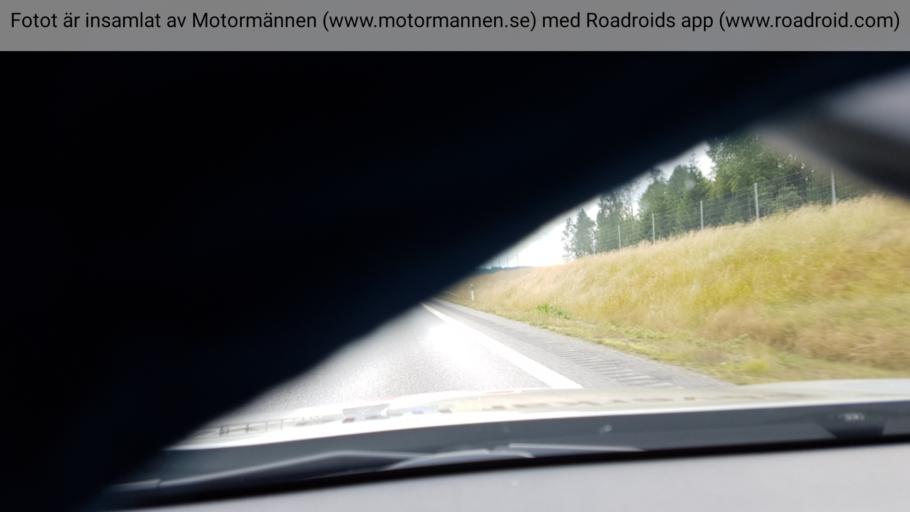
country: SE
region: Vaestra Goetaland
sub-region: Tanums Kommun
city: Tanumshede
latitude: 58.6252
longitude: 11.4475
